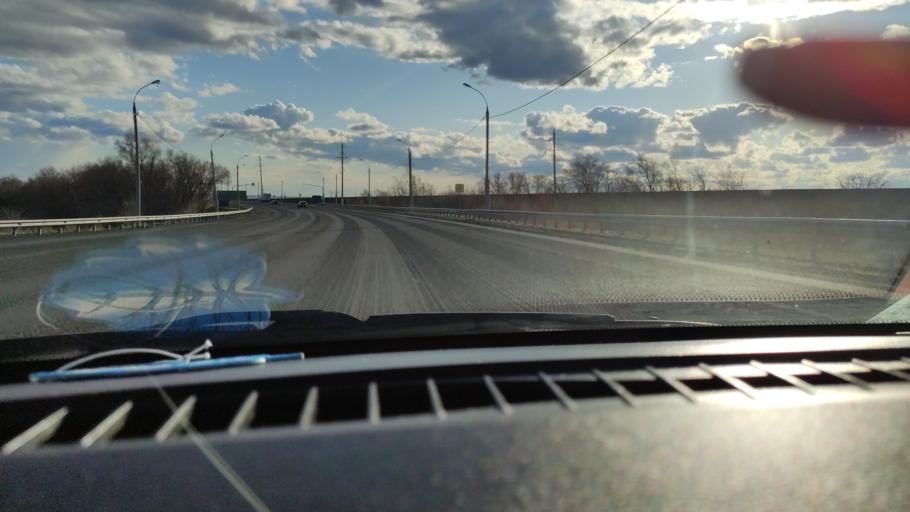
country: RU
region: Saratov
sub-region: Saratovskiy Rayon
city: Saratov
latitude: 51.7701
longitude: 46.0823
